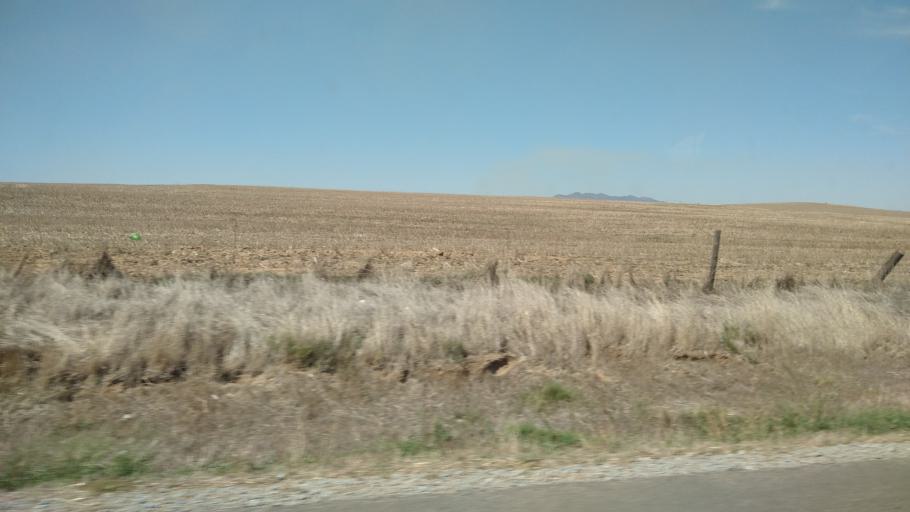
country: ZA
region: Western Cape
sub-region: West Coast District Municipality
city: Malmesbury
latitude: -33.3461
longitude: 18.6391
